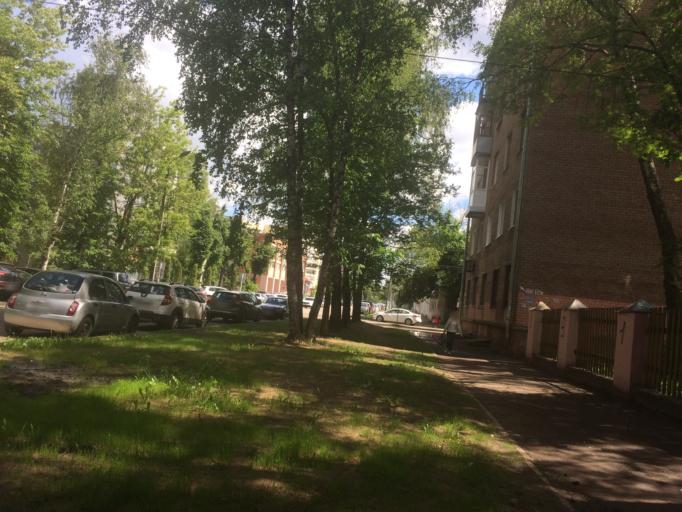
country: RU
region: Jaroslavl
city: Yaroslavl
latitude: 57.6300
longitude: 39.8536
